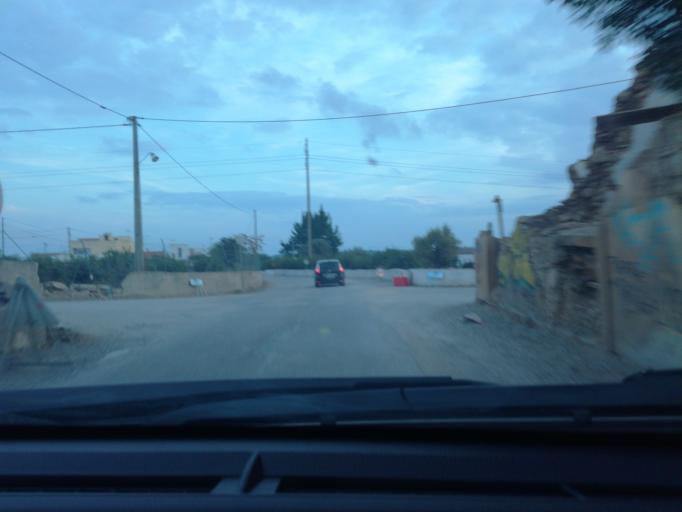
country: PT
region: Faro
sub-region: Olhao
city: Moncarapacho
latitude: 37.0821
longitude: -7.7823
